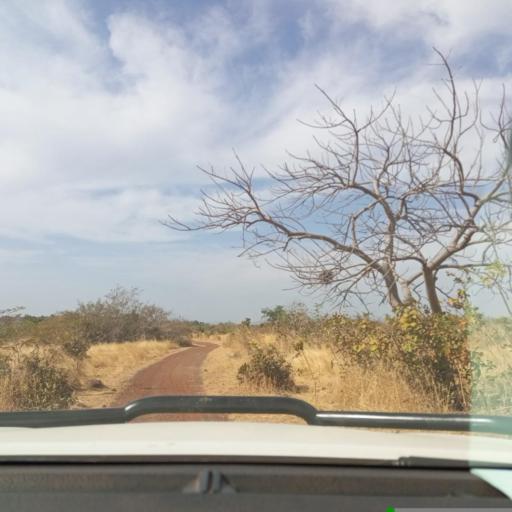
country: ML
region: Koulikoro
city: Kati
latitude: 12.7462
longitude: -8.2498
